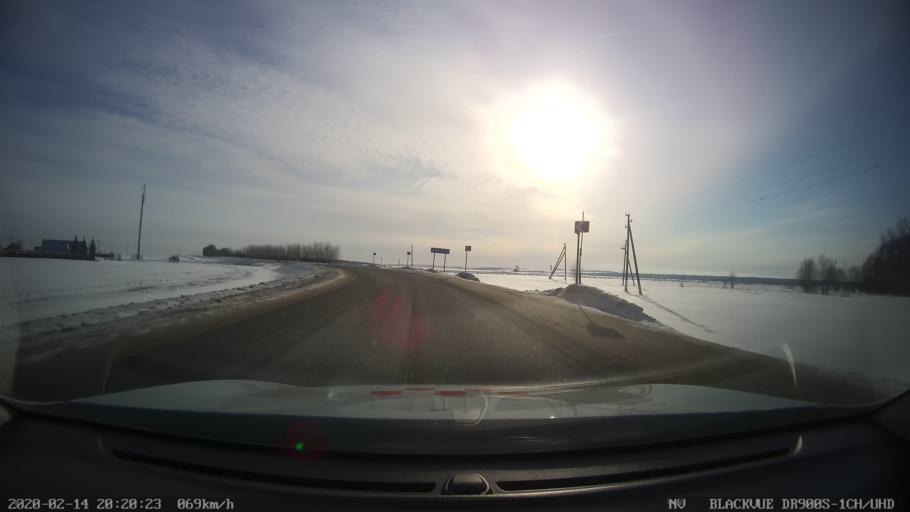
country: RU
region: Tatarstan
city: Verkhniy Uslon
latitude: 55.5577
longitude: 48.9053
